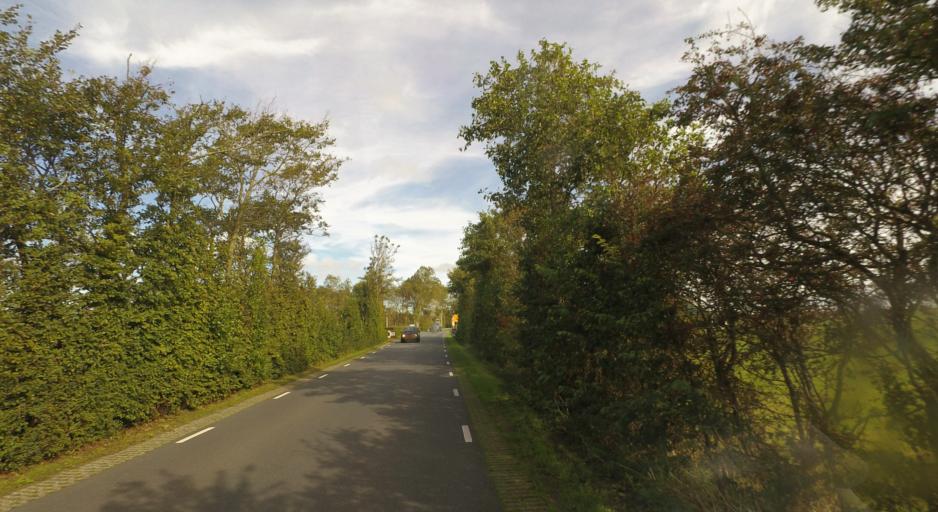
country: NL
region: Friesland
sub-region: Gemeente Ameland
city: Nes
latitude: 53.4473
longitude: 5.7856
